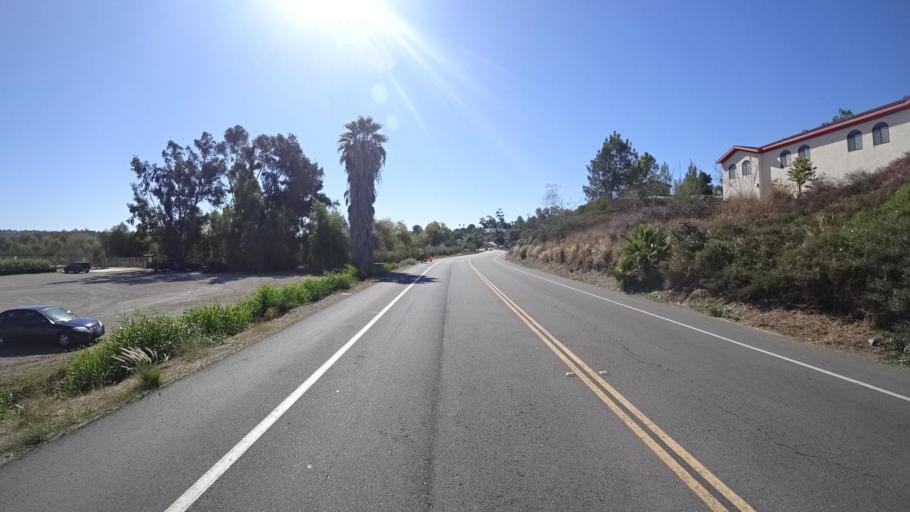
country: US
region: California
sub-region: San Diego County
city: Bonita
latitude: 32.6773
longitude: -117.0191
